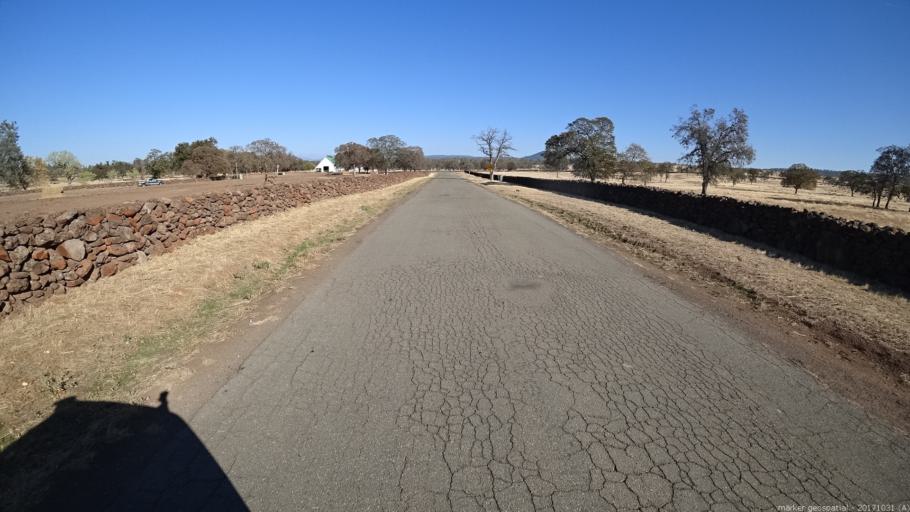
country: US
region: California
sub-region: Shasta County
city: Palo Cedro
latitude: 40.4626
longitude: -122.0899
